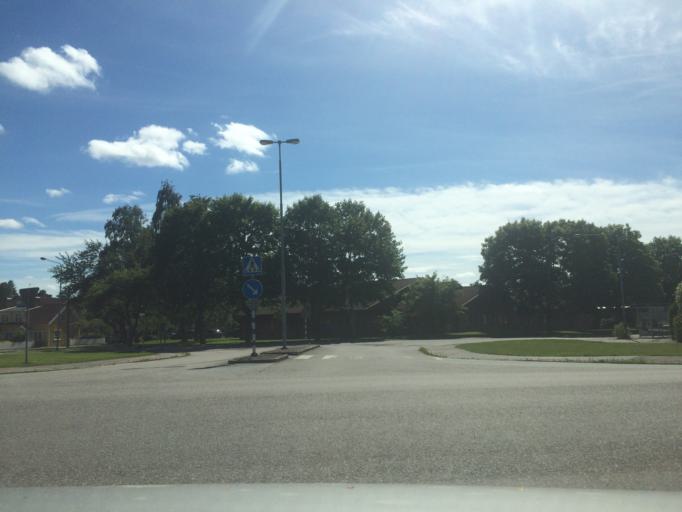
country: SE
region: Vaestra Goetaland
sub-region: Trollhattan
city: Trollhattan
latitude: 58.2886
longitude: 12.3212
